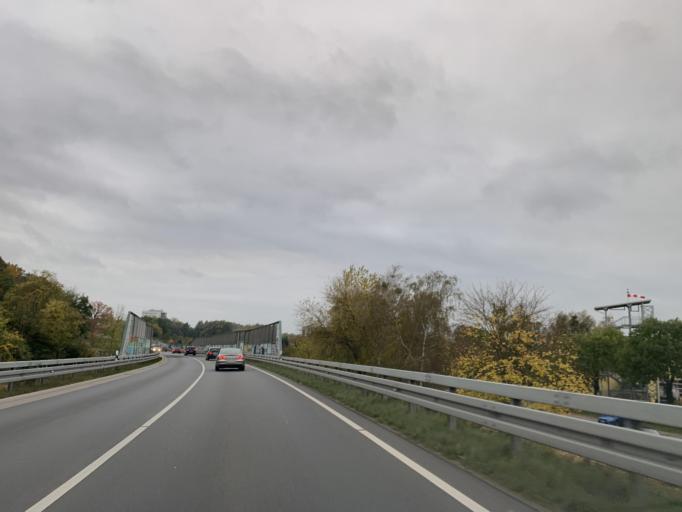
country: DE
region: Mecklenburg-Vorpommern
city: Neubrandenburg
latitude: 53.5549
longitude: 13.2800
